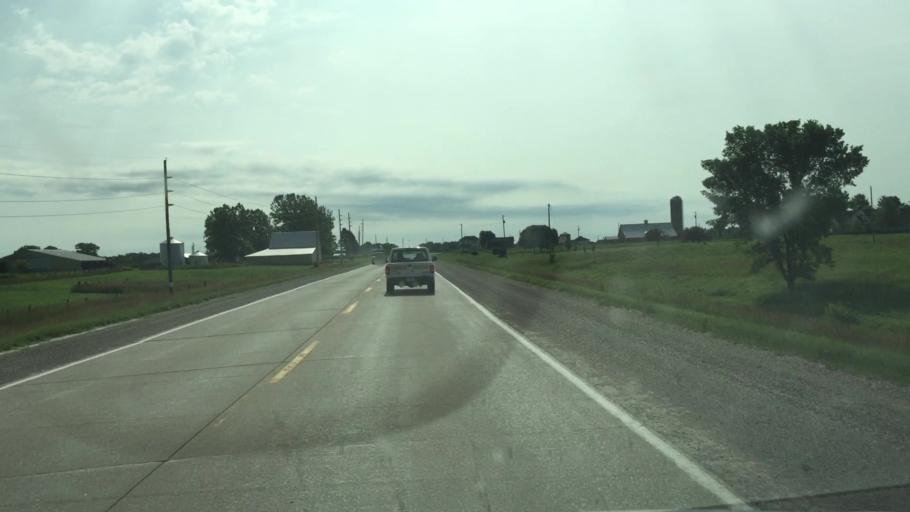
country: US
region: Illinois
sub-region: Hancock County
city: Nauvoo
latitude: 40.6314
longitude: -91.5065
